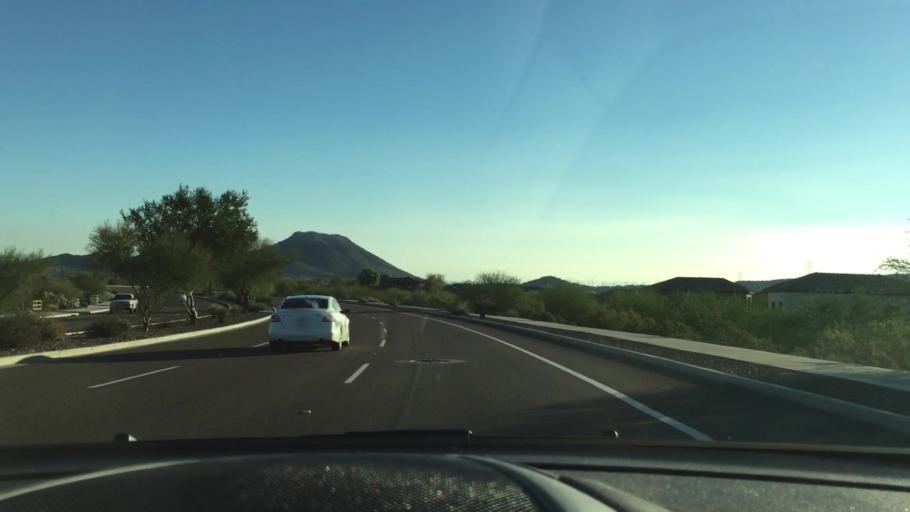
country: US
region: Arizona
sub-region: Maricopa County
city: Sun City
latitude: 33.7068
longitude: -112.2329
